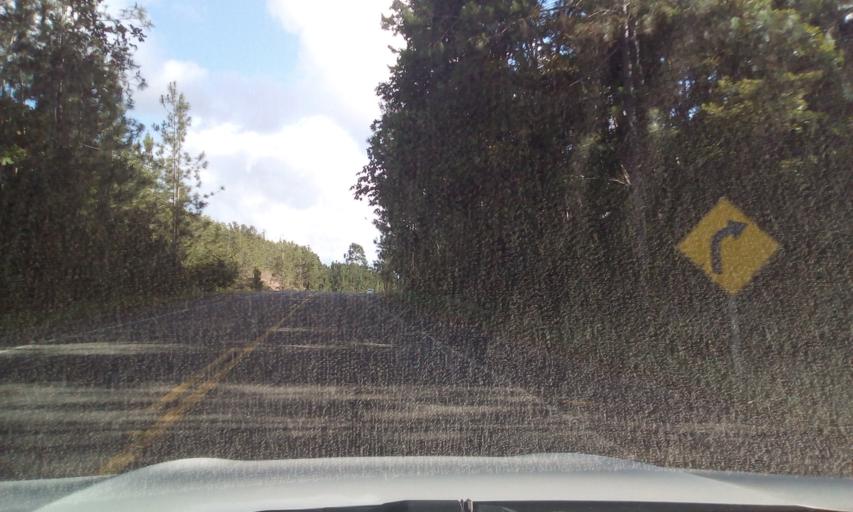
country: BR
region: Bahia
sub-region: Conde
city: Conde
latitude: -12.1057
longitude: -37.7834
